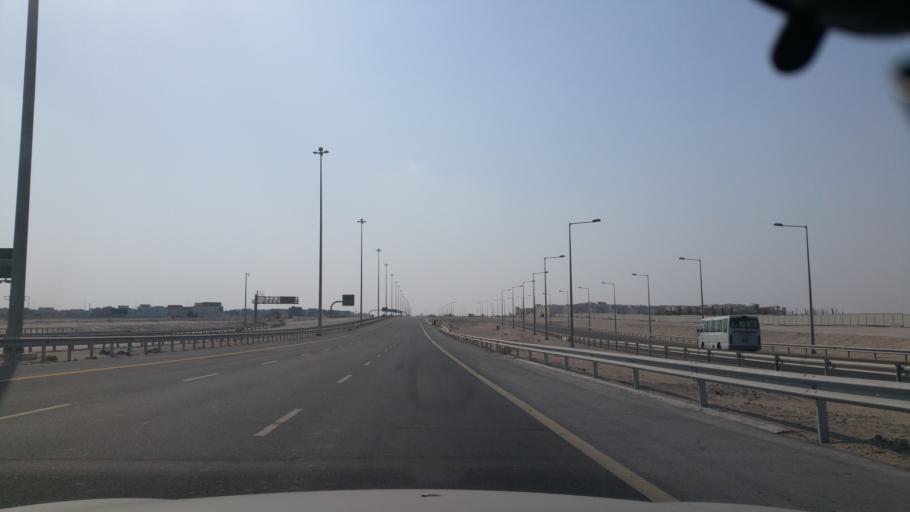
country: QA
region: Baladiyat Umm Salal
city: Umm Salal `Ali
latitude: 25.4571
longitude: 51.4742
